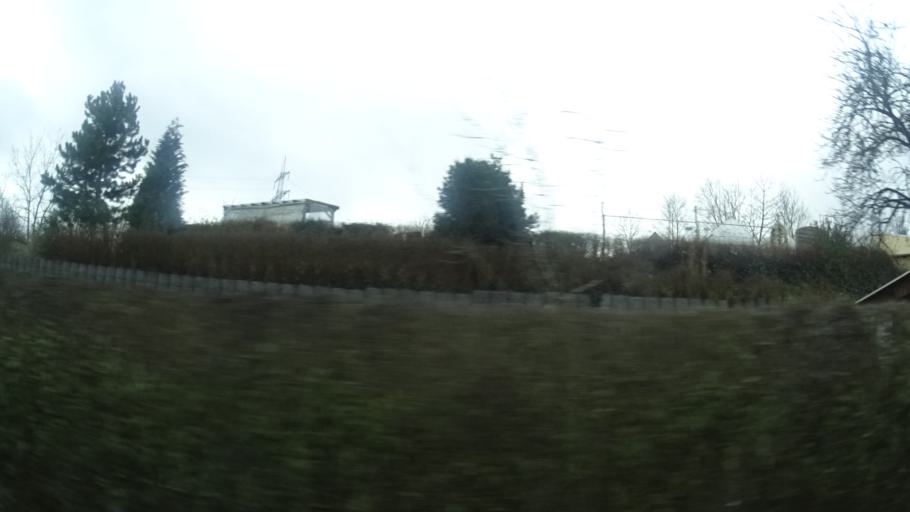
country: DE
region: Thuringia
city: Wittgendorf
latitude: 50.6024
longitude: 11.2471
